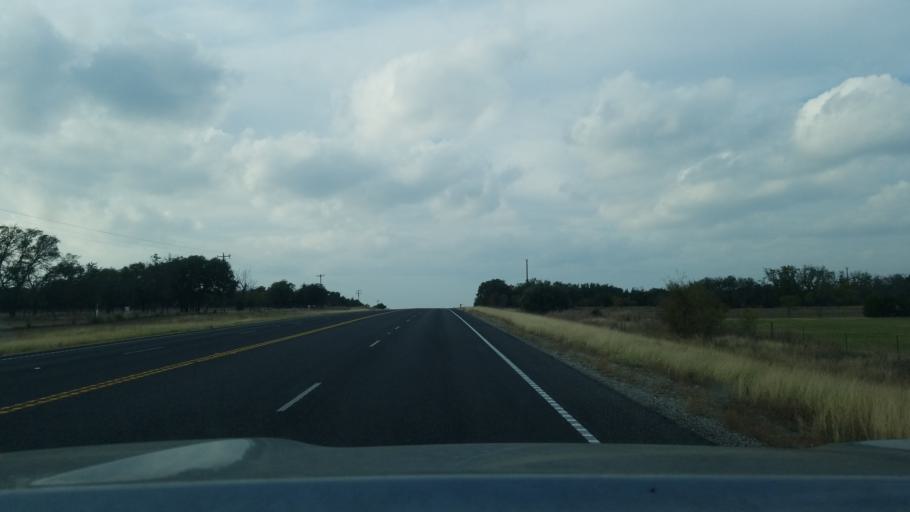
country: US
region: Texas
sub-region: Mills County
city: Goldthwaite
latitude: 31.3697
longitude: -98.5218
